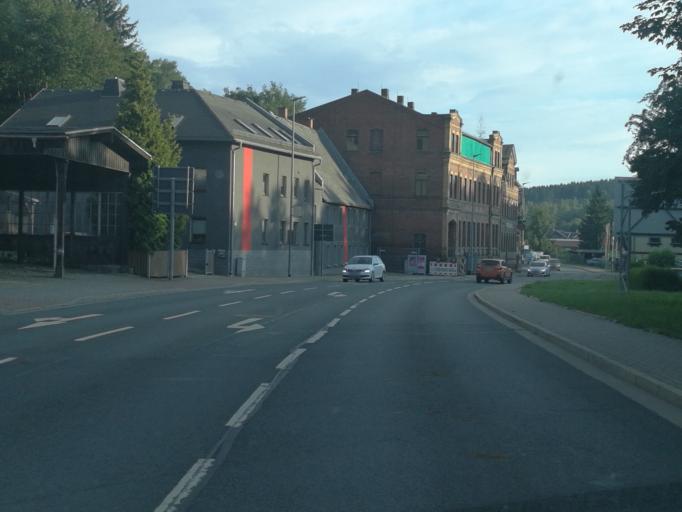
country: DE
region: Saxony
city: Adorf
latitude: 50.3219
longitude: 12.2574
